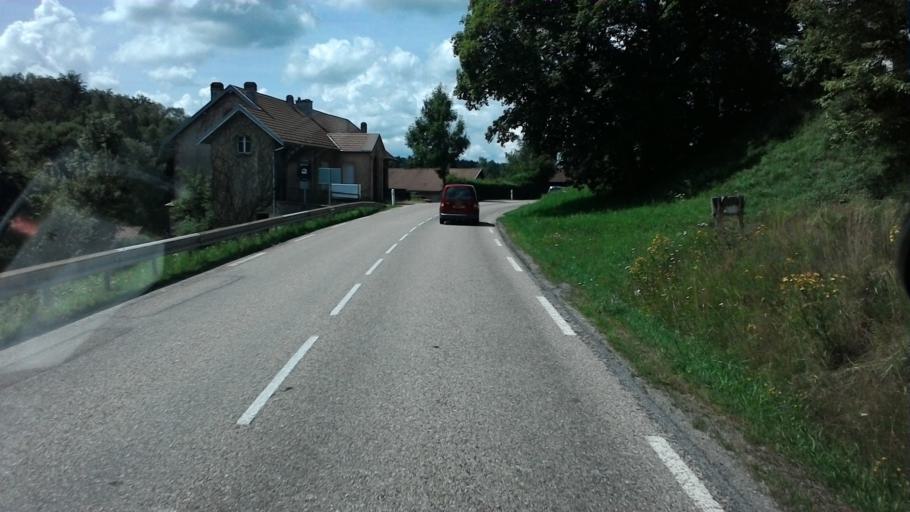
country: FR
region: Lorraine
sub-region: Departement des Vosges
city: Le Tholy
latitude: 48.0946
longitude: 6.7193
